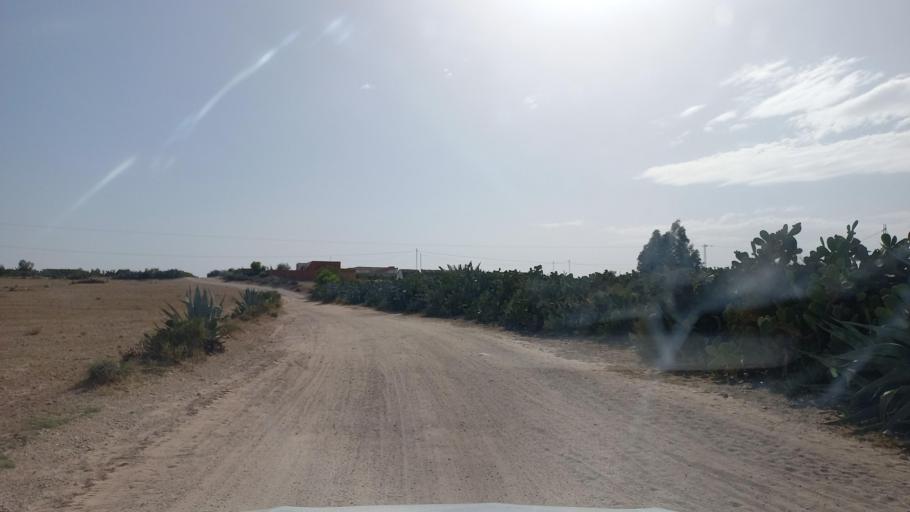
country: TN
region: Al Qasrayn
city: Kasserine
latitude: 35.2775
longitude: 8.9449
